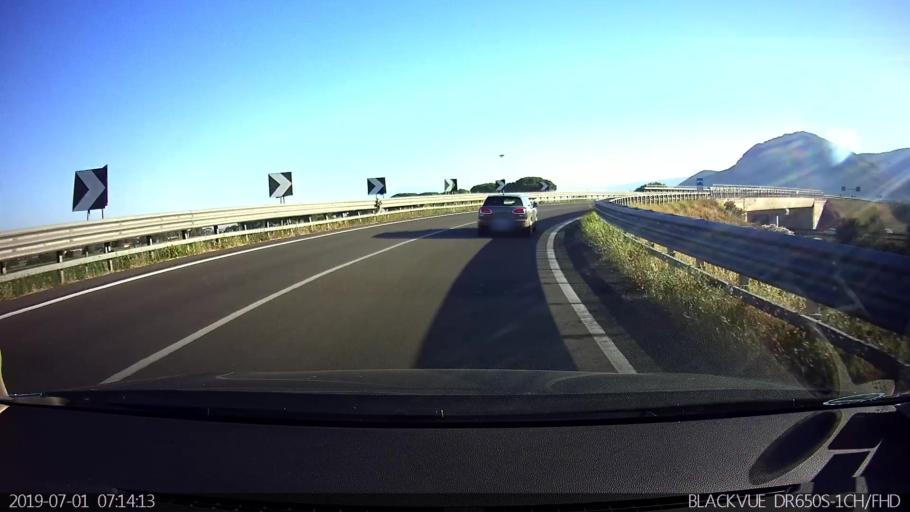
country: IT
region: Latium
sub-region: Provincia di Latina
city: Borgo Hermada
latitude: 41.3208
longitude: 13.1830
